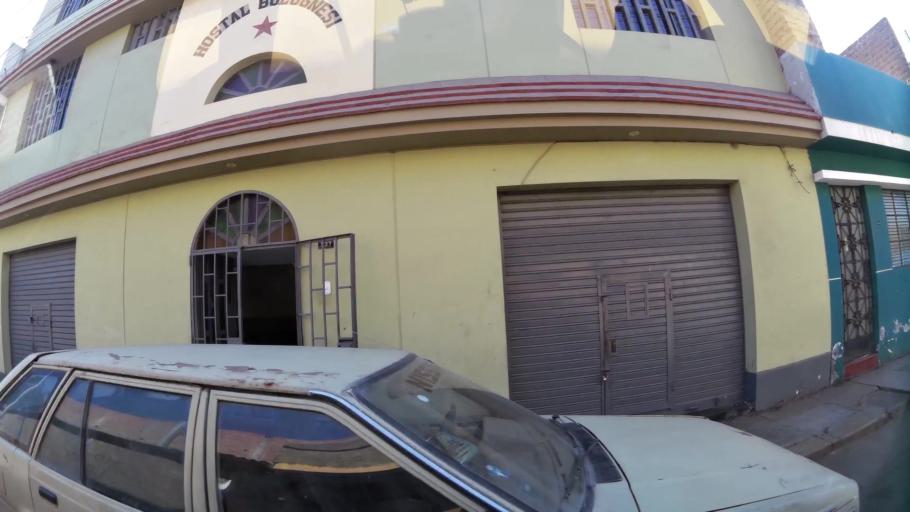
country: PE
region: Ica
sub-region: Provincia de Ica
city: Ica
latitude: -14.0680
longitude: -75.7263
